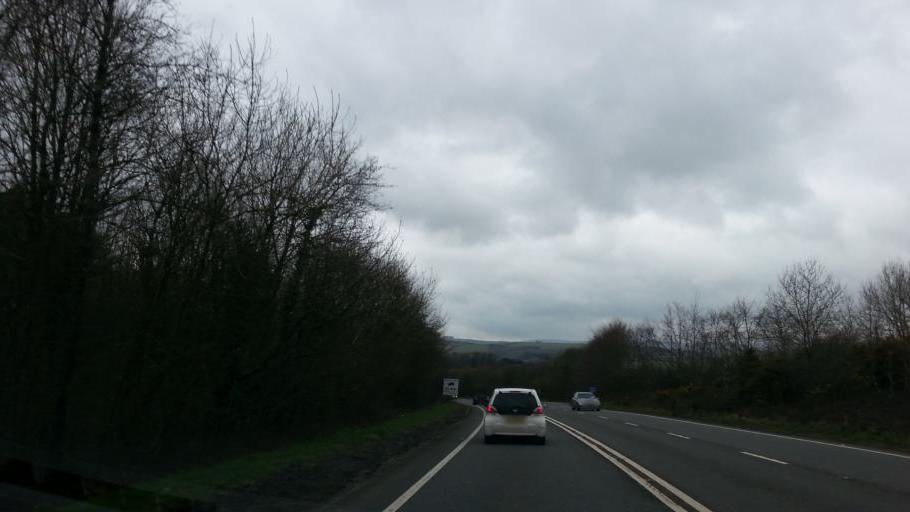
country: GB
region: England
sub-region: Devon
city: South Molton
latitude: 51.0081
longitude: -3.7516
